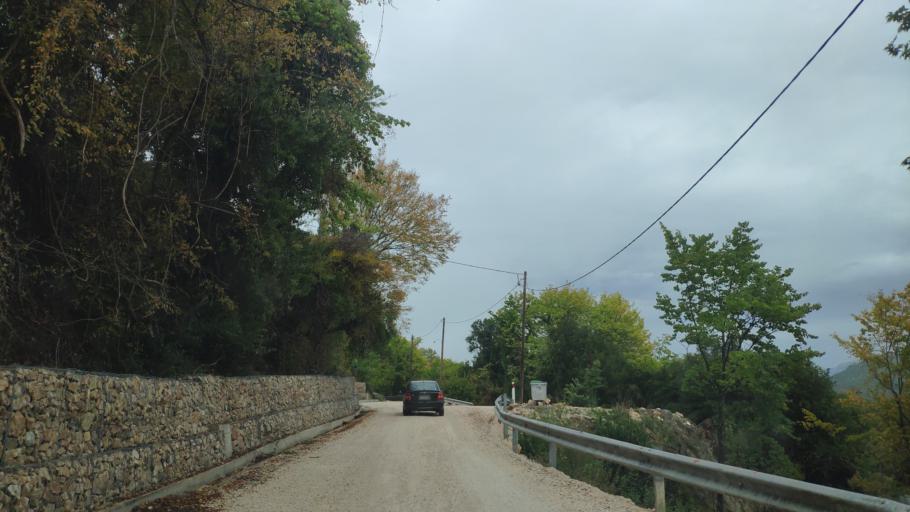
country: GR
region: Epirus
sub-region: Nomos Thesprotias
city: Paramythia
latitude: 39.4665
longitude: 20.6717
